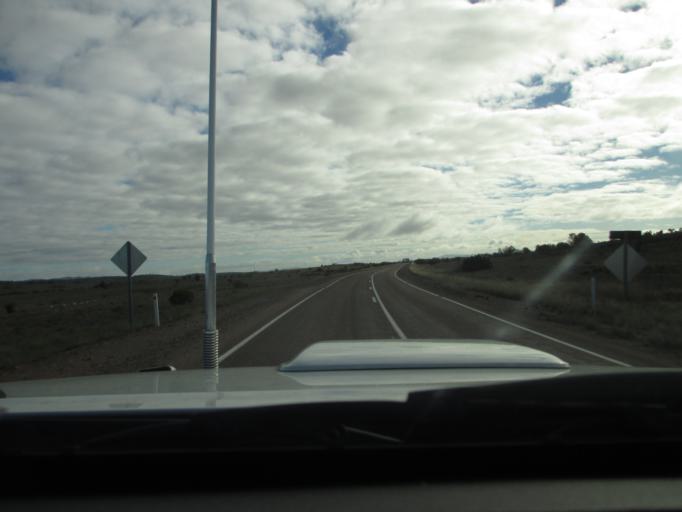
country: AU
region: South Australia
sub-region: Peterborough
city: Peterborough
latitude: -32.5497
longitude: 138.5603
